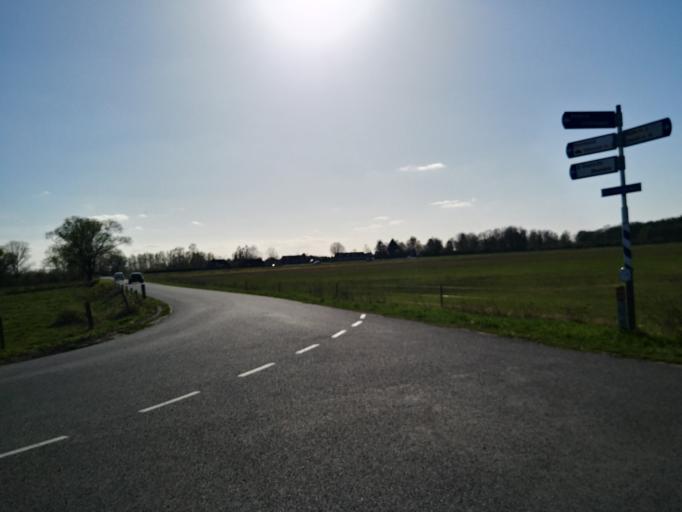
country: NL
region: Overijssel
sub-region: Gemeente Olst-Wijhe
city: Olst
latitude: 52.3645
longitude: 6.0966
